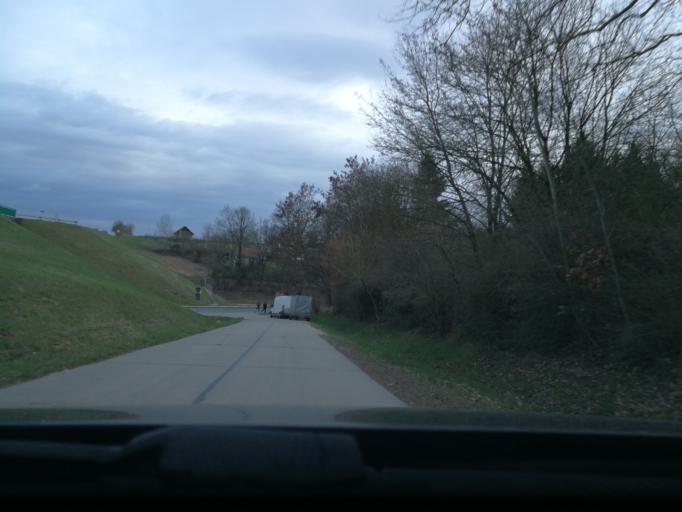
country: DE
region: Bavaria
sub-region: Regierungsbezirk Mittelfranken
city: Obermichelbach
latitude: 49.5244
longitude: 10.9578
